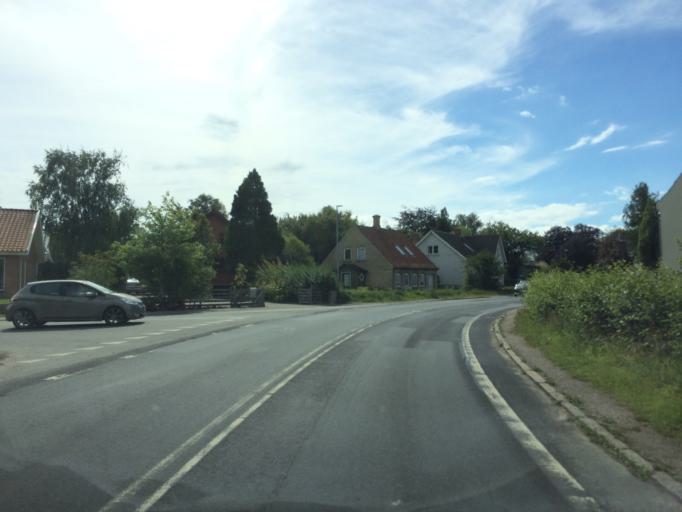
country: DK
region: South Denmark
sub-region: Faaborg-Midtfyn Kommune
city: Faaborg
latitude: 55.1972
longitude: 10.2496
